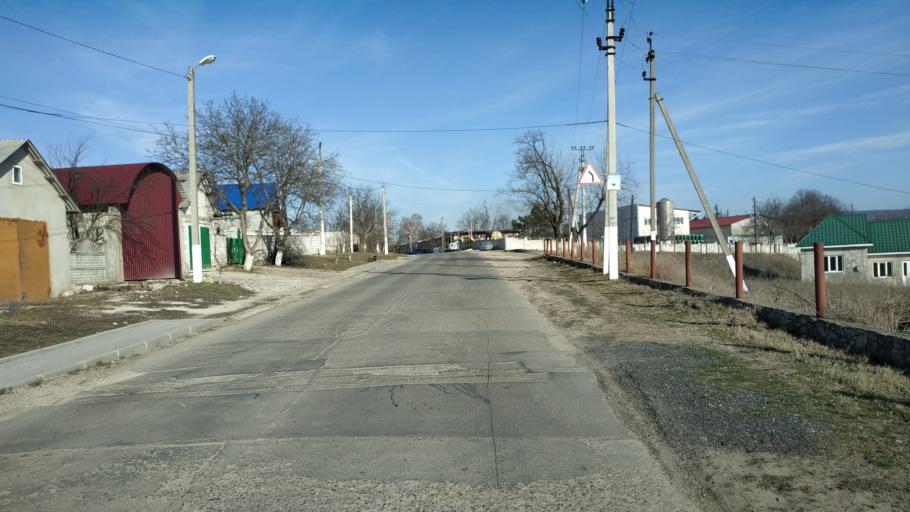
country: MD
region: Chisinau
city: Vatra
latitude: 47.0029
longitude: 28.6717
